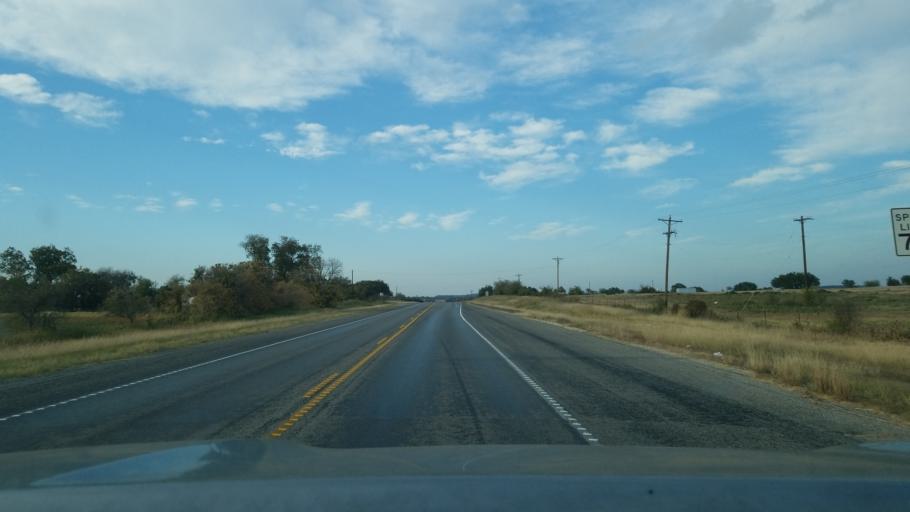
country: US
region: Texas
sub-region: Brown County
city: Lake Brownwood
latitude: 31.9875
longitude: -98.9208
